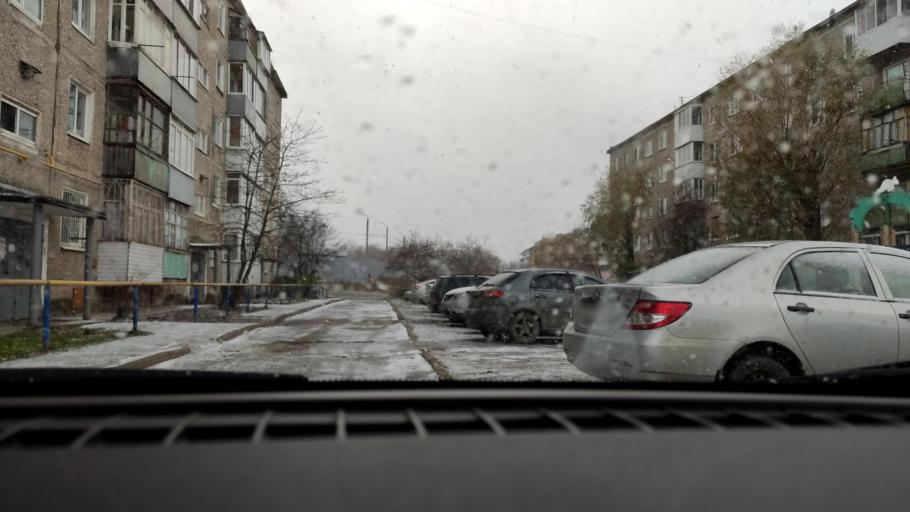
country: RU
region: Perm
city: Kondratovo
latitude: 57.9473
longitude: 56.0805
